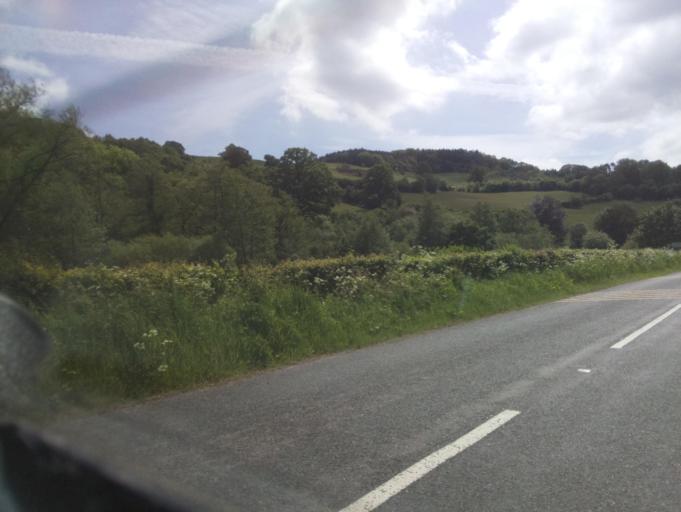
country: GB
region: England
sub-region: Herefordshire
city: Llanrothal
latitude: 51.8788
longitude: -2.7875
